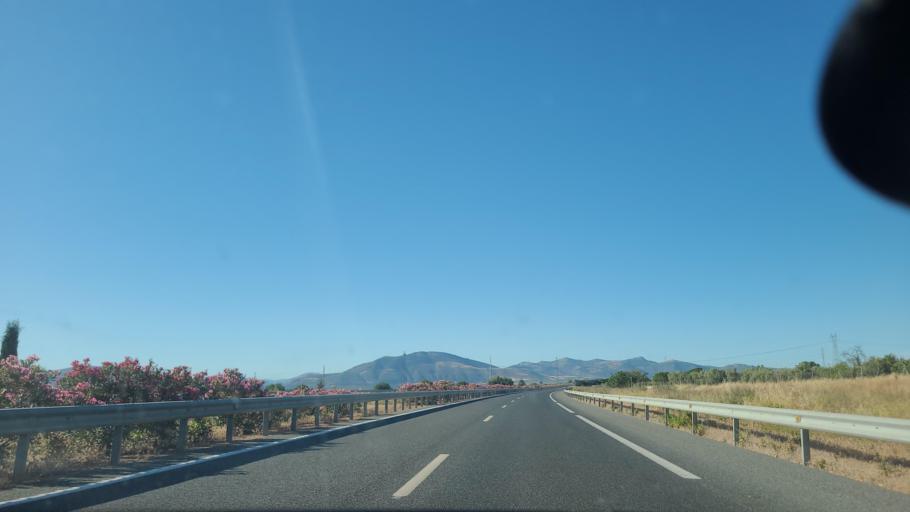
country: ES
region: Andalusia
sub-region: Provincia de Granada
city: Albolote
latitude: 37.2566
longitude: -3.6630
